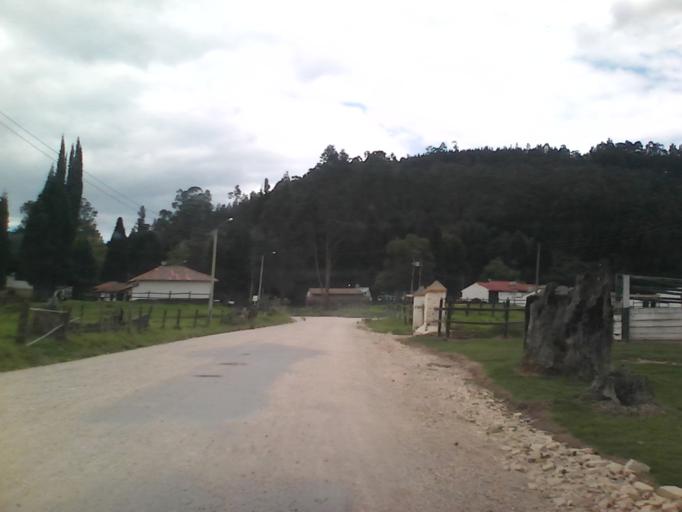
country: CO
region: Boyaca
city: Duitama
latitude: 5.8088
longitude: -73.0659
